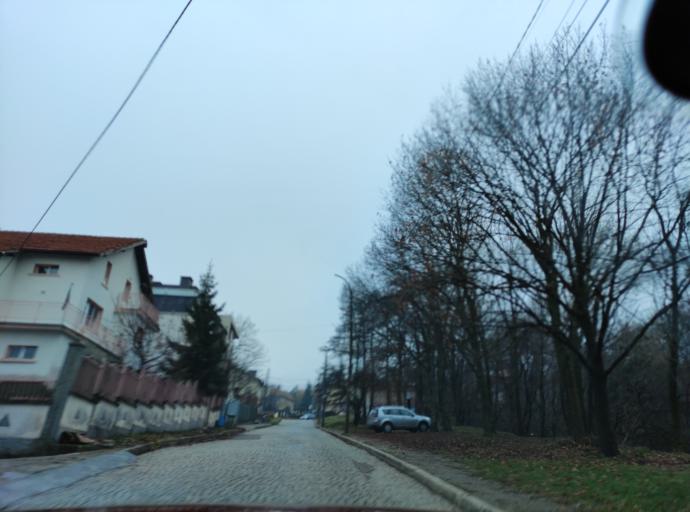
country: BG
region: Sofia-Capital
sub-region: Stolichna Obshtina
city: Sofia
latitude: 42.6268
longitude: 23.3079
